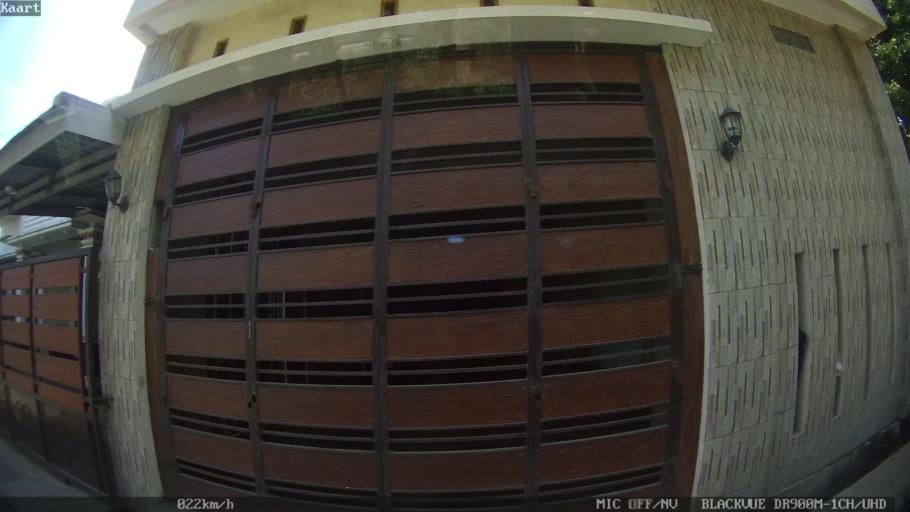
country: ID
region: Lampung
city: Kedaton
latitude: -5.3386
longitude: 105.2725
